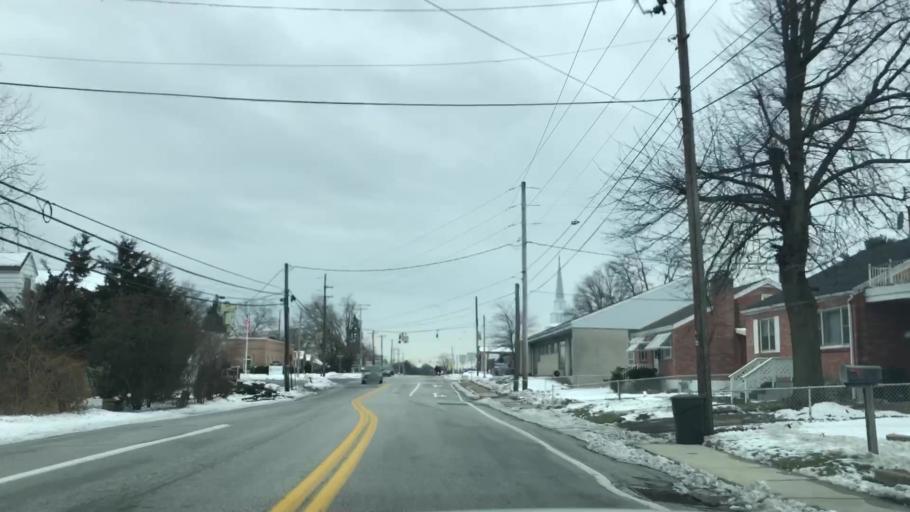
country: US
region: Pennsylvania
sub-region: Dauphin County
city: Colonial Park
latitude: 40.2932
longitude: -76.8061
